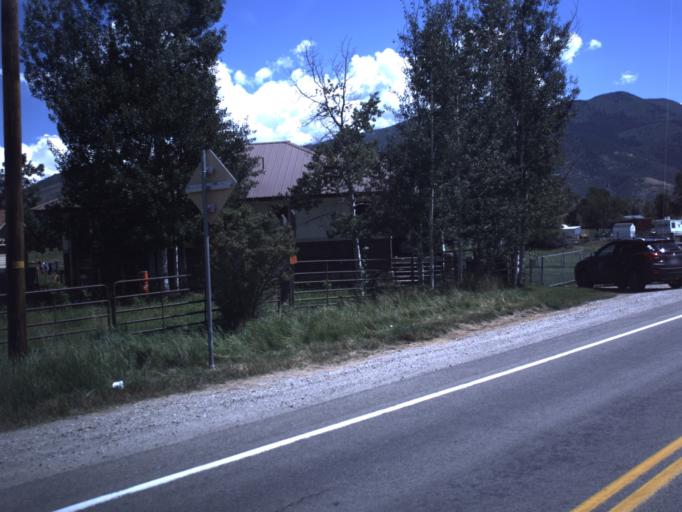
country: US
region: Utah
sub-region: Summit County
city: Oakley
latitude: 40.7123
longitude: -111.2994
